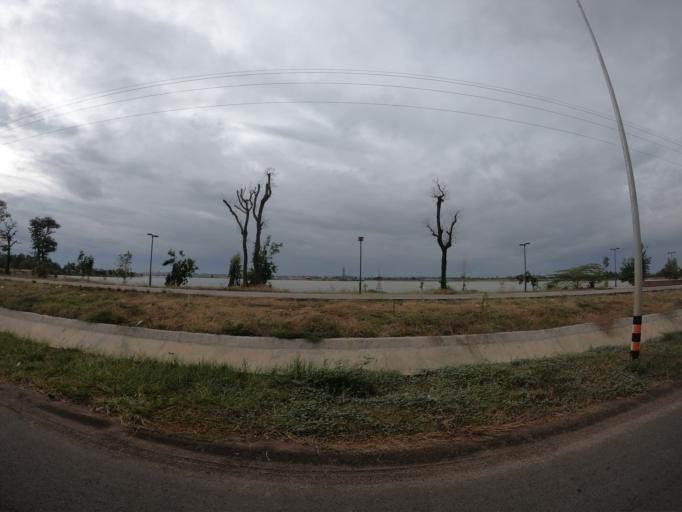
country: TH
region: Roi Et
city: Thawat Buri
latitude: 16.0826
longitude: 103.7206
